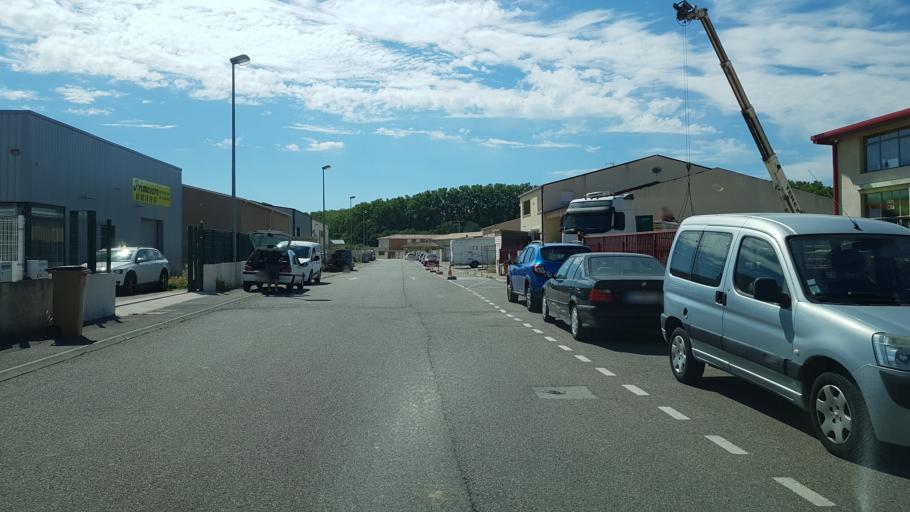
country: FR
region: Provence-Alpes-Cote d'Azur
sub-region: Departement des Bouches-du-Rhone
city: Saint-Martin-de-Crau
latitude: 43.6424
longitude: 4.7971
